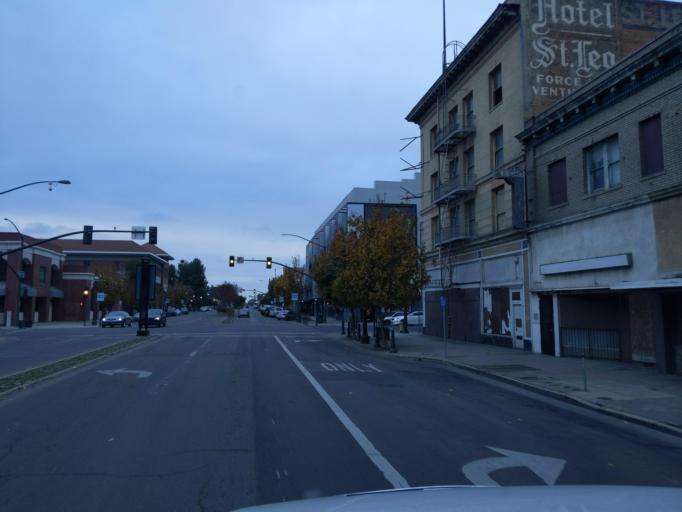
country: US
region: California
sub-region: San Joaquin County
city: Stockton
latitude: 37.9545
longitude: -121.2855
